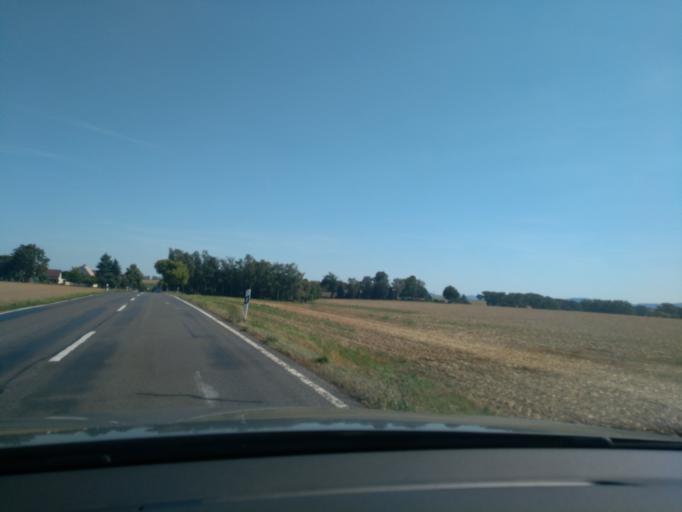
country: DE
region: Saxony
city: Crostwitz
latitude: 51.2199
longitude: 14.2427
